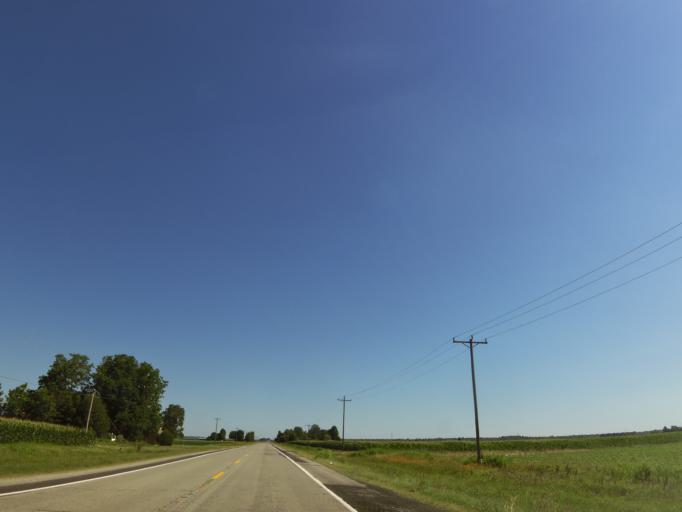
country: US
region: Arkansas
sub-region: Clay County
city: Piggott
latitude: 36.3882
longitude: -90.1484
